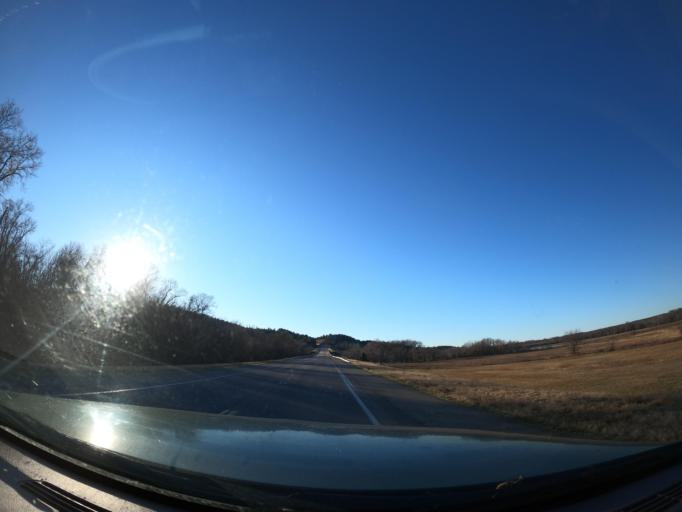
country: US
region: Oklahoma
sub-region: Pittsburg County
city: Hartshorne
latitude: 34.8916
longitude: -95.4450
